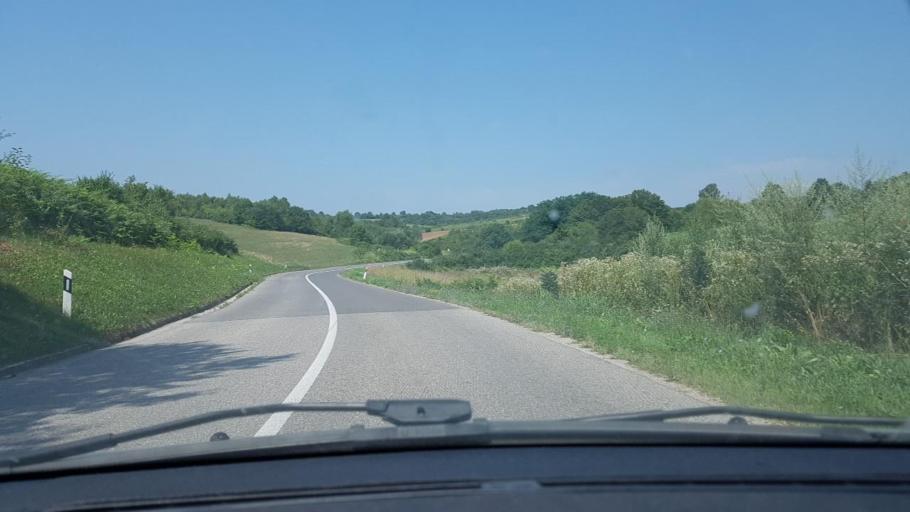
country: BA
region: Federation of Bosnia and Herzegovina
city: Velika Kladusa
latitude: 45.2036
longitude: 15.7768
